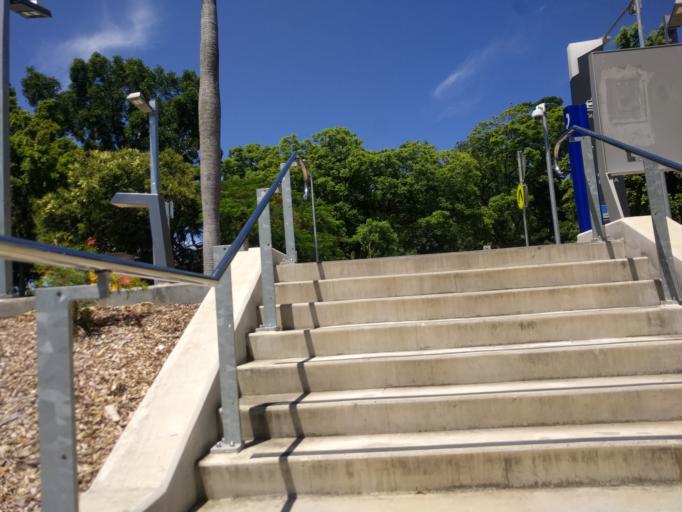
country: AU
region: Queensland
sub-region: Brisbane
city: South Brisbane
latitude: -27.4969
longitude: 153.0191
